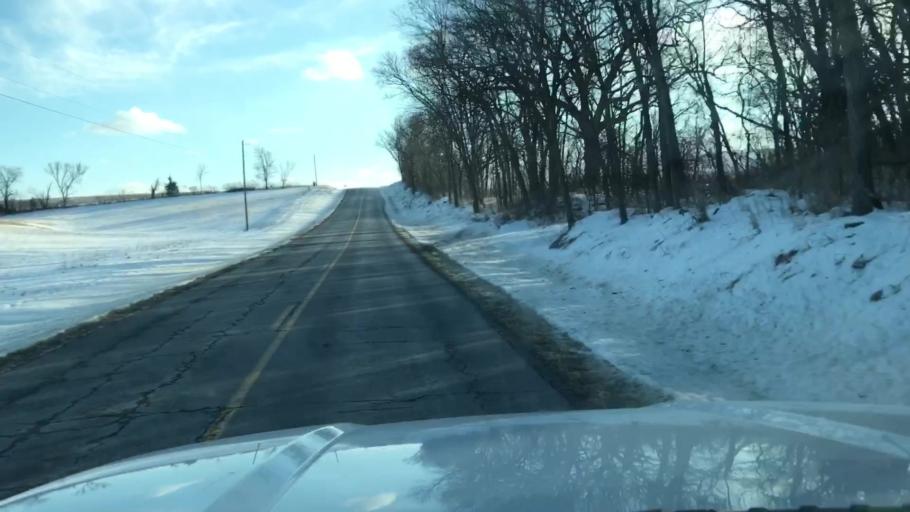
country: US
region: Missouri
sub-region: Holt County
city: Oregon
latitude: 40.0662
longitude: -94.9748
